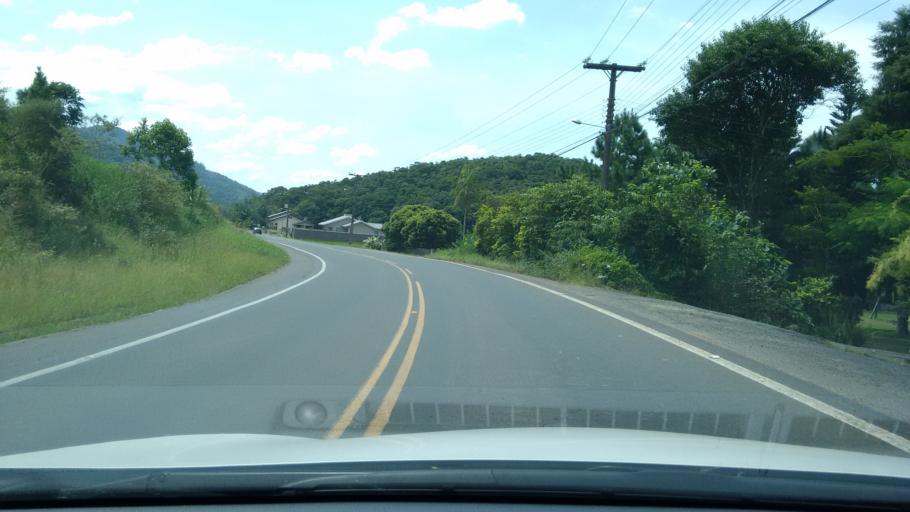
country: BR
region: Santa Catarina
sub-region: Rodeio
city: Gavea
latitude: -26.8859
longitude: -49.3479
